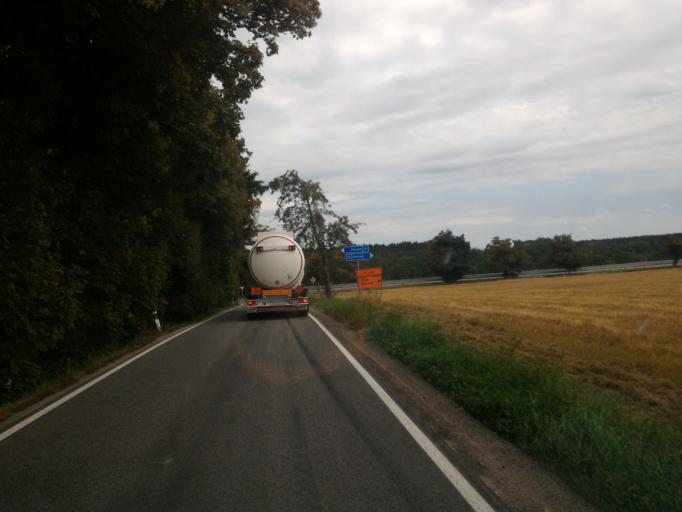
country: CZ
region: Vysocina
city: Zeletava
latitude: 49.2046
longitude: 15.6151
